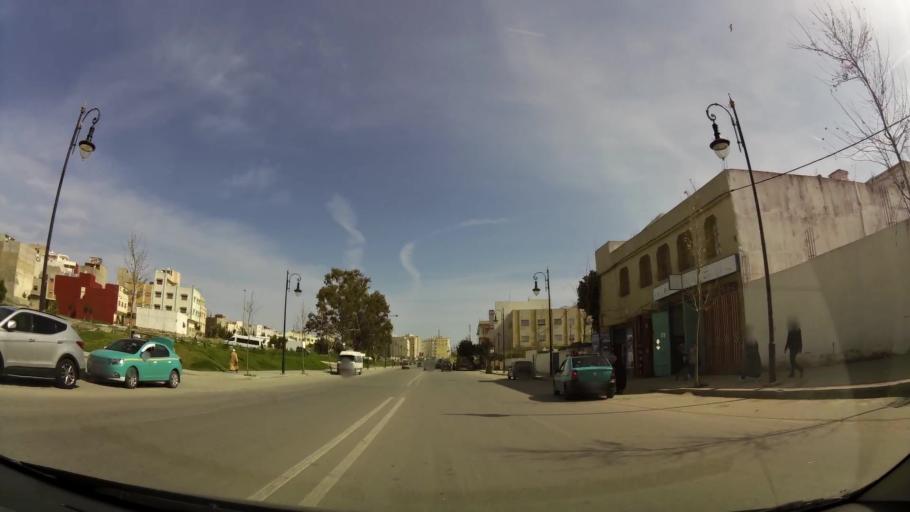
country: MA
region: Tanger-Tetouan
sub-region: Tanger-Assilah
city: Tangier
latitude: 35.7276
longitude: -5.8033
